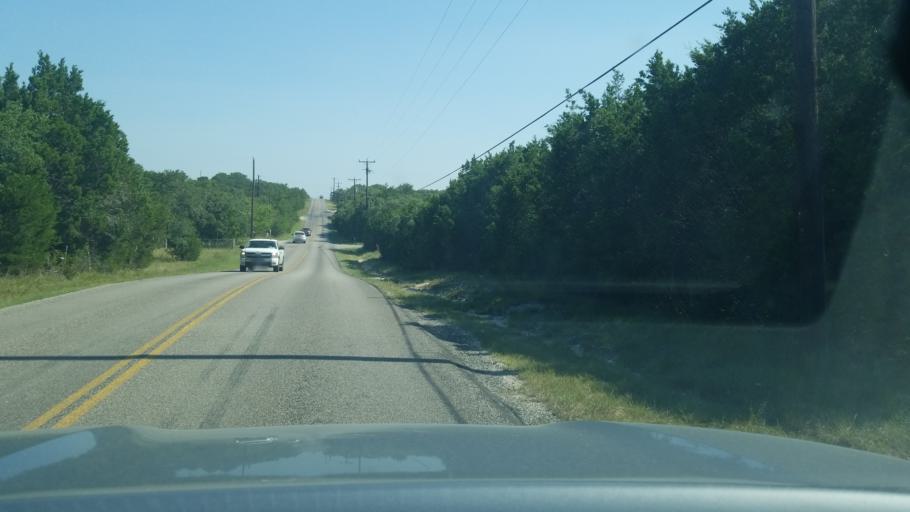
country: US
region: Texas
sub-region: Comal County
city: Bulverde
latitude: 29.7598
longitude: -98.5128
